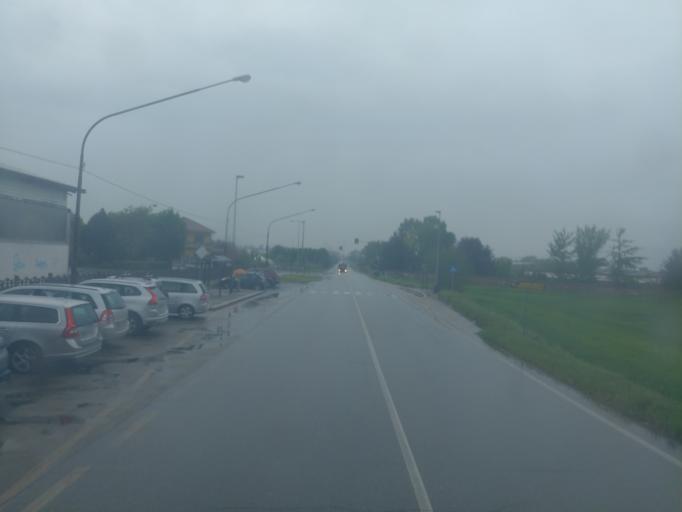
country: IT
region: Piedmont
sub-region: Provincia di Torino
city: La Loggia
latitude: 44.9424
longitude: 7.6702
